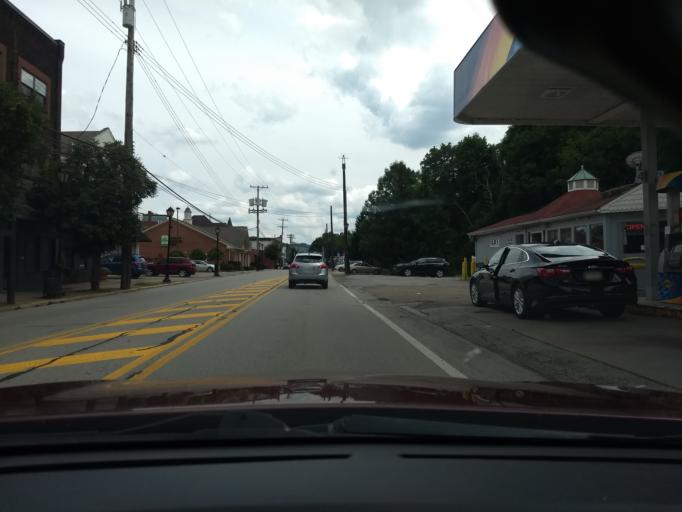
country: US
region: Pennsylvania
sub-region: Allegheny County
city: Aspinwall
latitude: 40.4894
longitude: -79.9034
